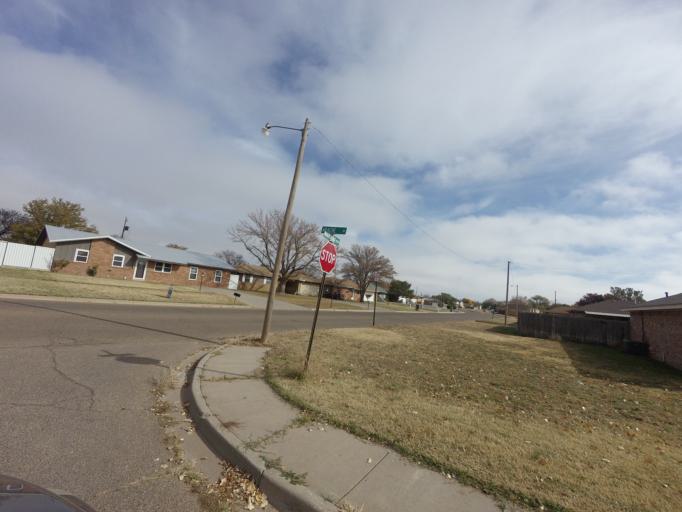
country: US
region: New Mexico
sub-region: Curry County
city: Clovis
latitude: 34.4274
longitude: -103.2307
